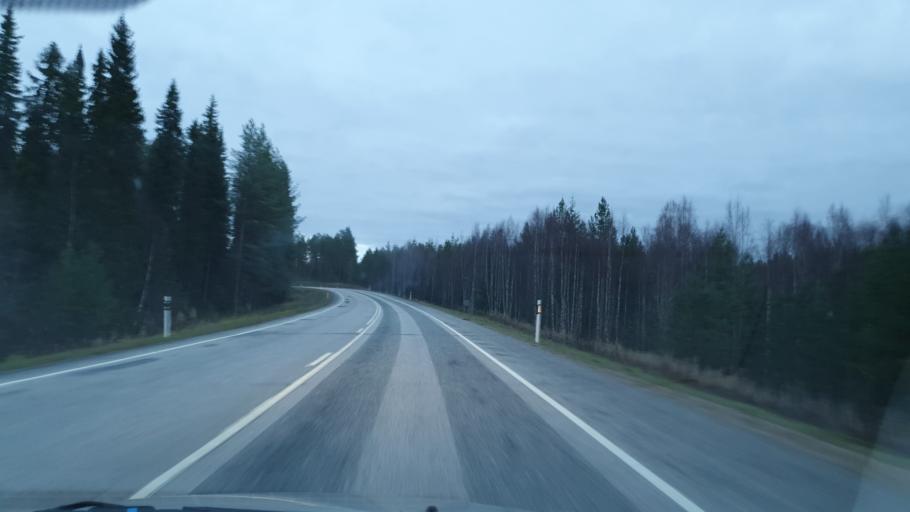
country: FI
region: Kainuu
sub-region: Kehys-Kainuu
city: Hyrynsalmi
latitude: 64.5724
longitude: 28.3840
